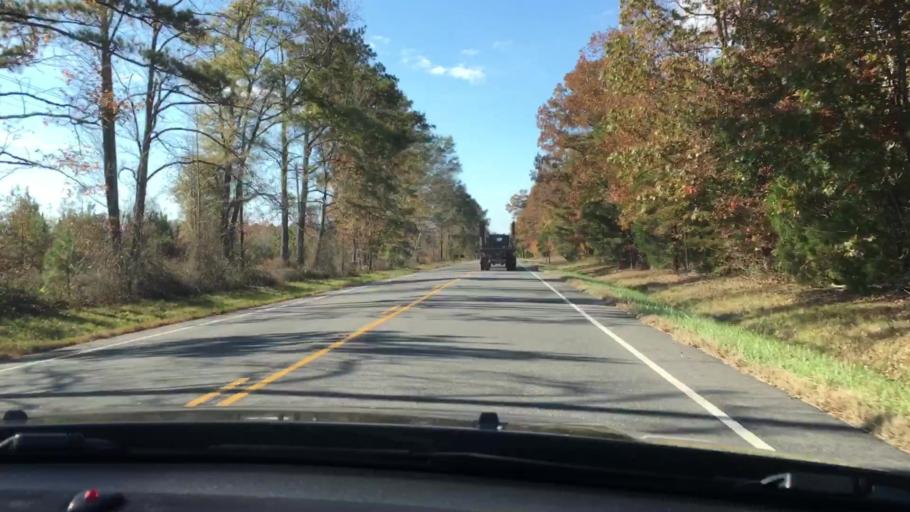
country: US
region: Virginia
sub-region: King William County
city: Central Garage
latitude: 37.7929
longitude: -77.2342
